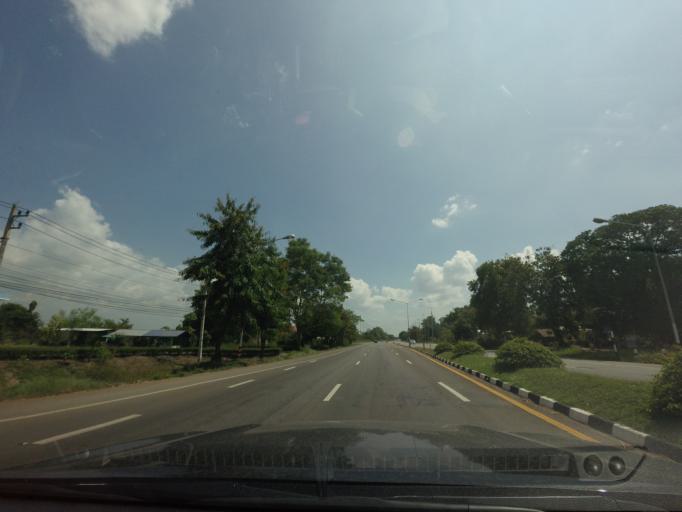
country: TH
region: Phetchabun
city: Nong Phai
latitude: 16.0992
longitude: 101.0461
